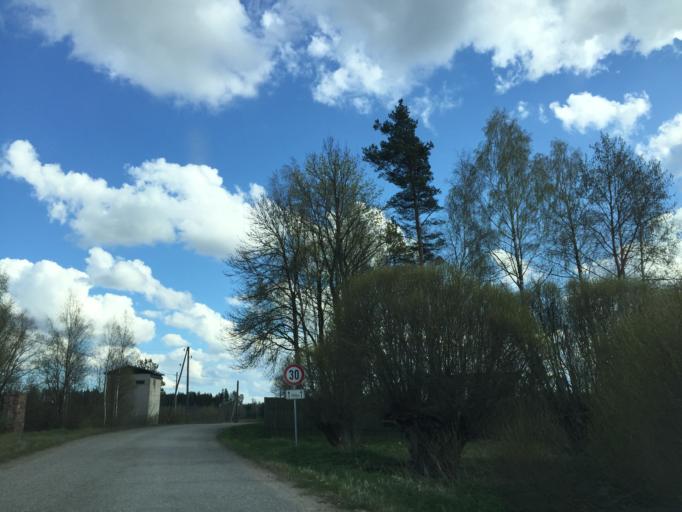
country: LV
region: Beverina
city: Murmuiza
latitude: 57.4682
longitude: 25.4978
